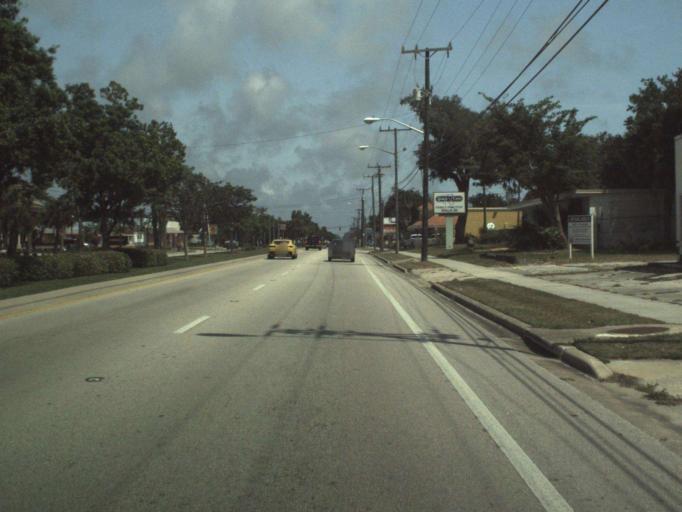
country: US
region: Florida
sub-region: Volusia County
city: Holly Hill
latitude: 29.2367
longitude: -81.0366
